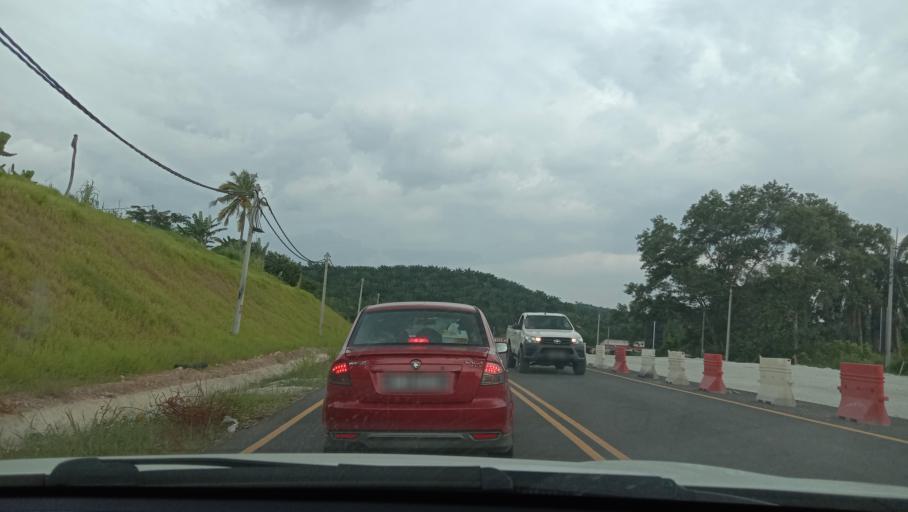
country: MY
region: Selangor
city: Batu Arang
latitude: 3.2627
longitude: 101.4598
